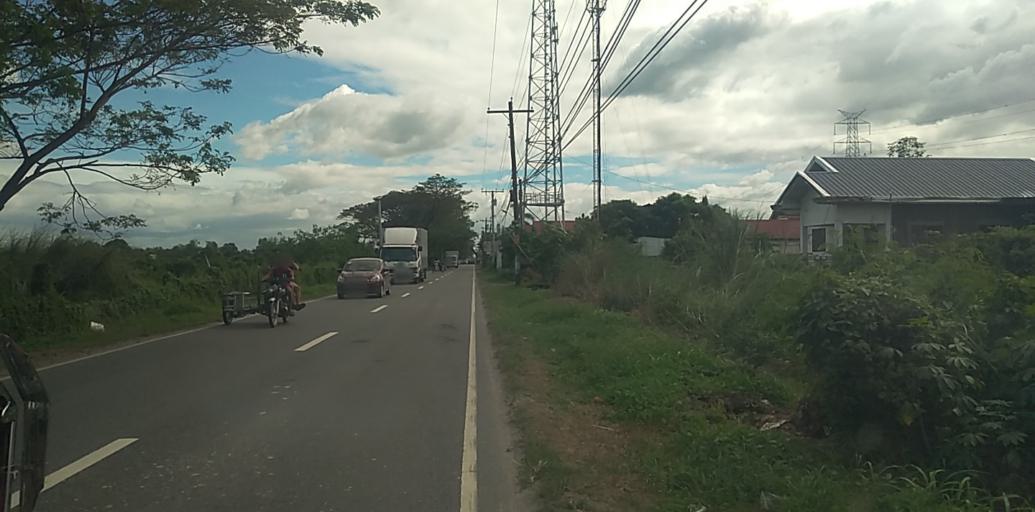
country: PH
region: Central Luzon
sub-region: Province of Pampanga
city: Arenas
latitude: 15.1801
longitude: 120.6776
